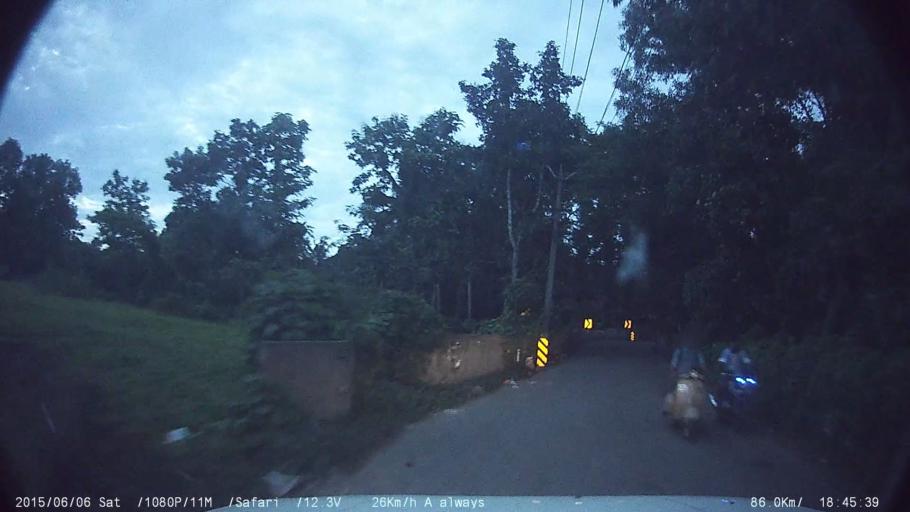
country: IN
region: Kerala
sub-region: Pattanamtitta
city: Tiruvalla
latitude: 9.4085
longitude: 76.5590
